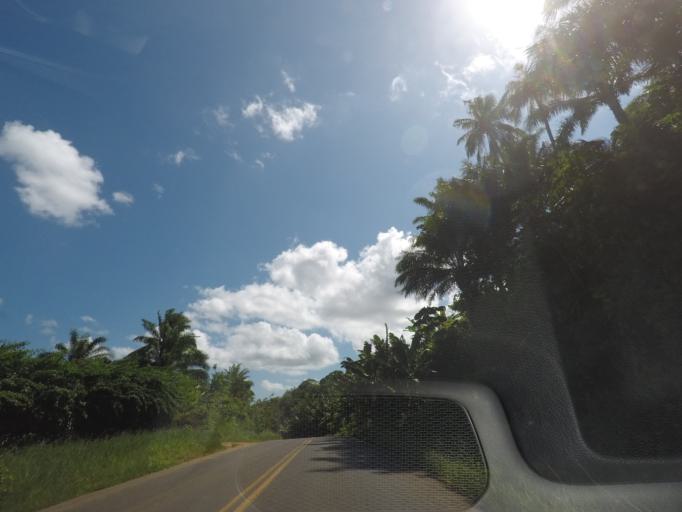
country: BR
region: Bahia
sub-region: Taperoa
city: Taperoa
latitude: -13.5745
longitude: -39.1059
